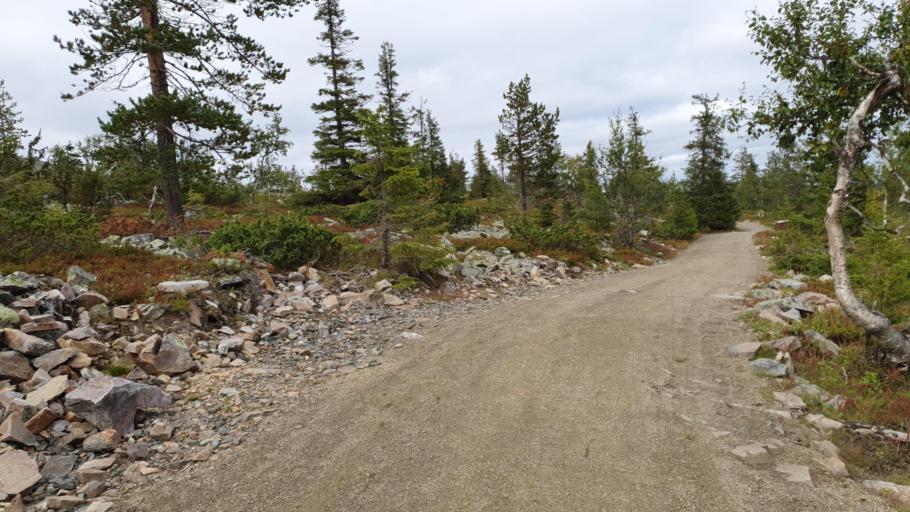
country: FI
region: Lapland
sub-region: Tunturi-Lappi
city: Kolari
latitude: 67.5657
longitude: 24.2602
